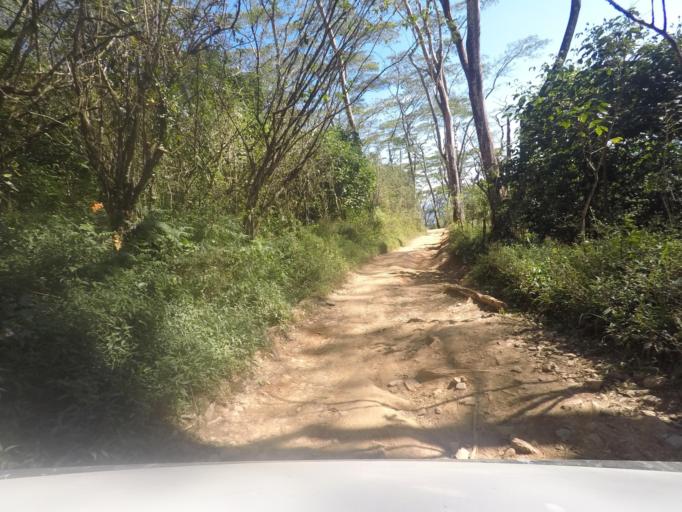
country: TL
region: Ermera
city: Gleno
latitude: -8.7330
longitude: 125.3418
